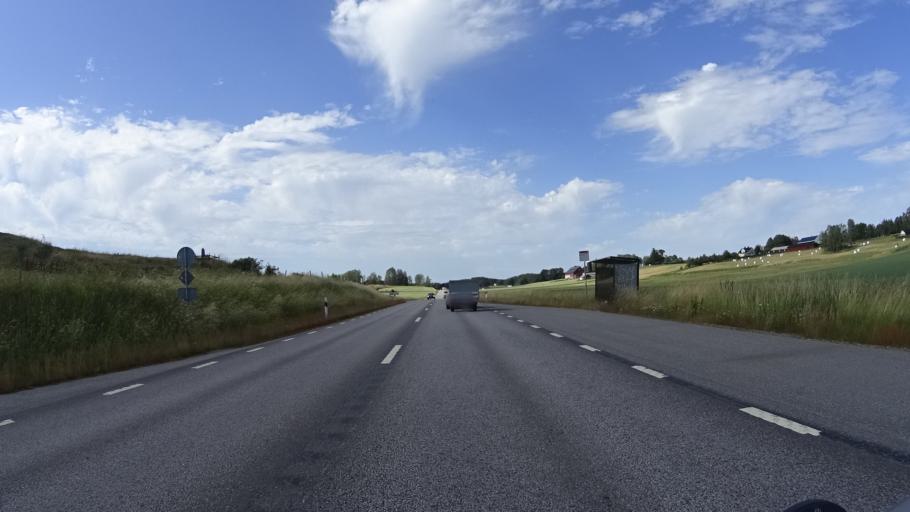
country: SE
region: OEstergoetland
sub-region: Linkopings Kommun
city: Linghem
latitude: 58.3414
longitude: 15.8454
